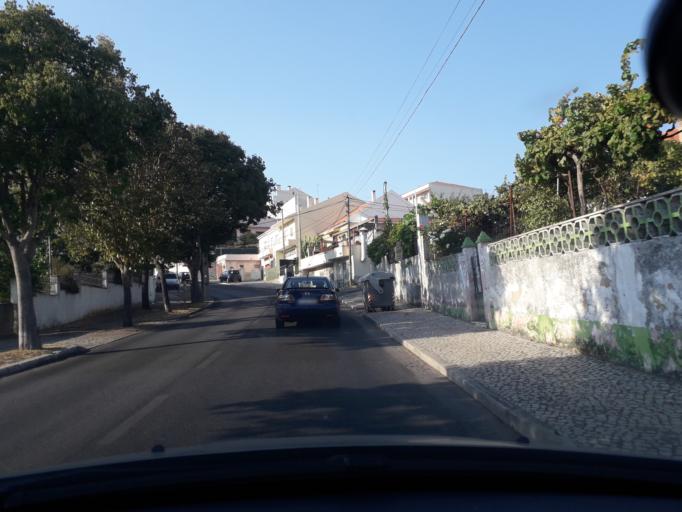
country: PT
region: Lisbon
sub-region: Odivelas
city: Famoes
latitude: 38.7792
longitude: -9.2155
